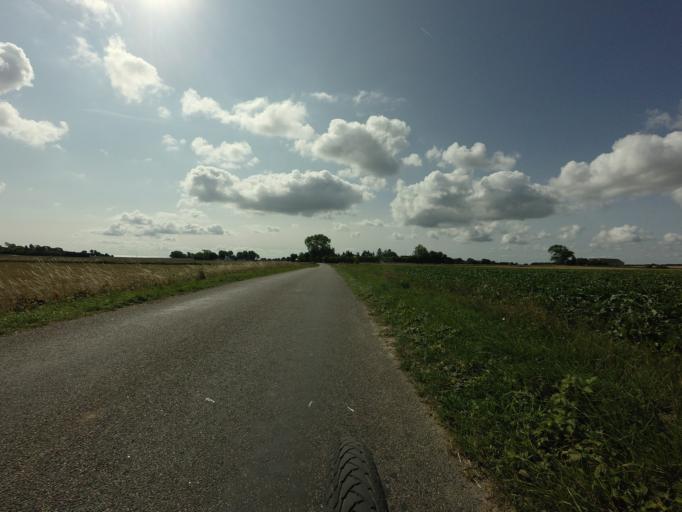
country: DK
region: Zealand
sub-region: Vordingborg Kommune
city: Stege
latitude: 54.9690
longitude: 12.3391
